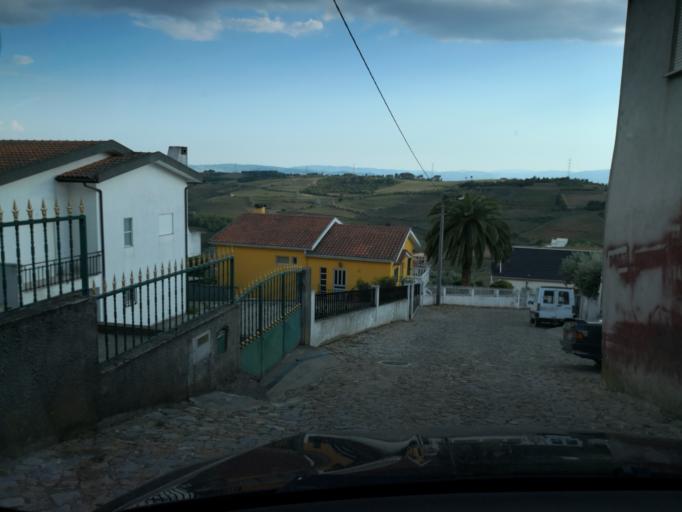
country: PT
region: Vila Real
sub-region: Sabrosa
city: Vilela
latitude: 41.2117
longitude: -7.6642
